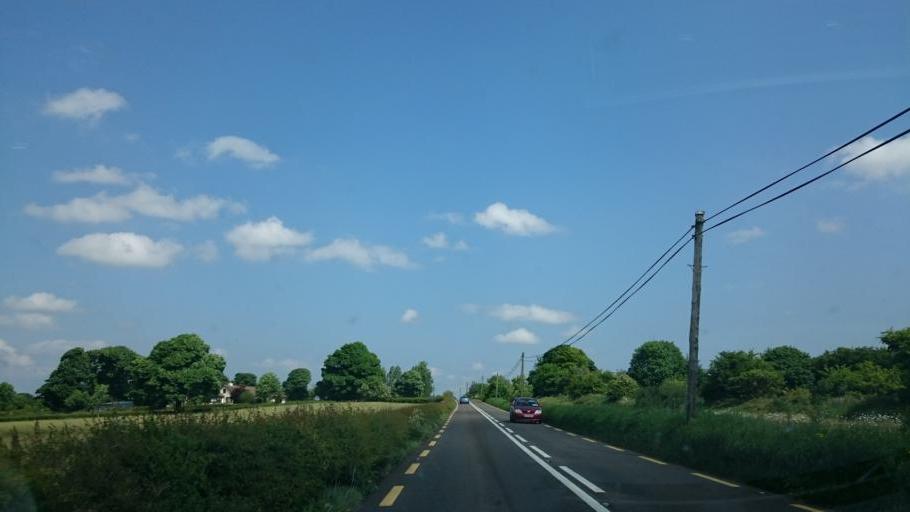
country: IE
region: Connaught
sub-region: Sligo
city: Tobercurry
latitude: 54.0228
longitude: -8.7551
